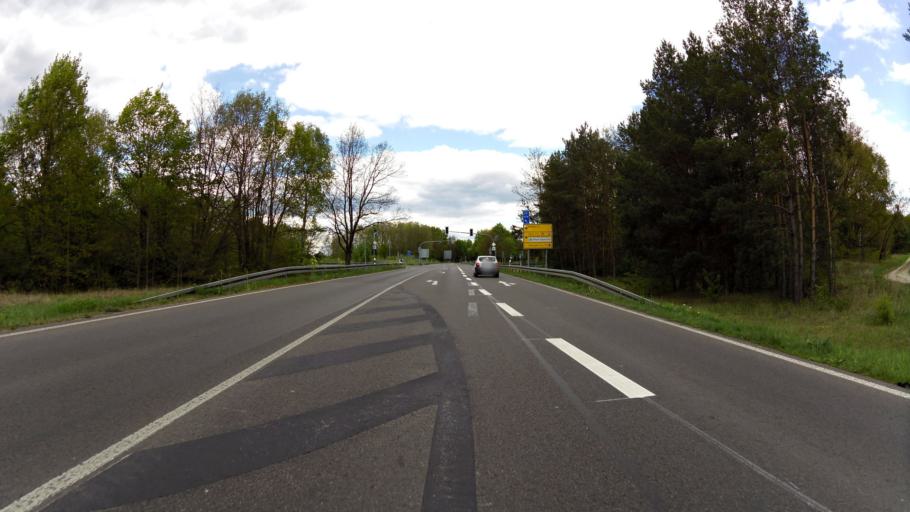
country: DE
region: Brandenburg
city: Furstenwalde
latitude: 52.3805
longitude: 14.0866
